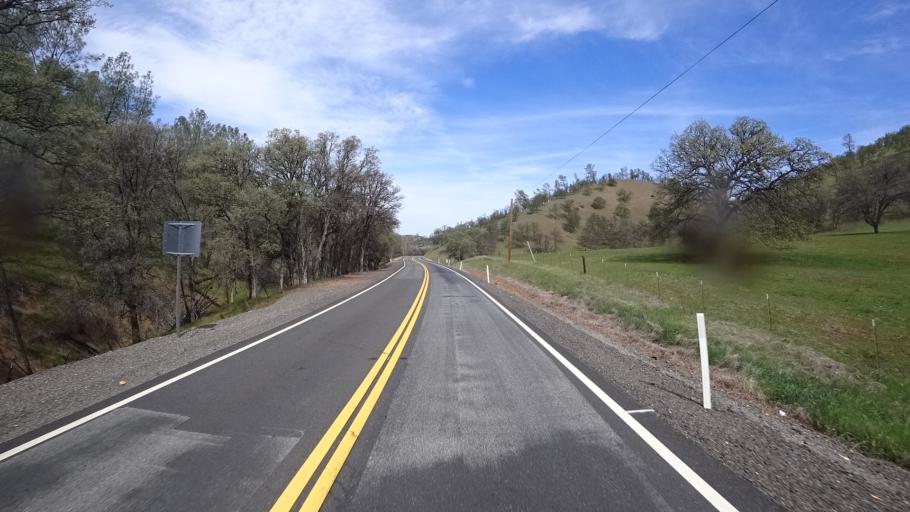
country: US
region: California
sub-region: Glenn County
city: Willows
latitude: 39.6034
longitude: -122.5077
